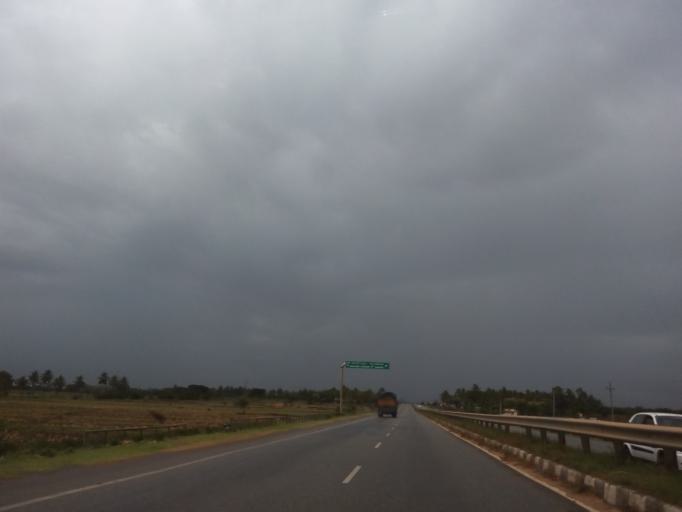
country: IN
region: Karnataka
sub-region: Davanagere
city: Harihar
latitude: 14.4493
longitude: 75.8807
